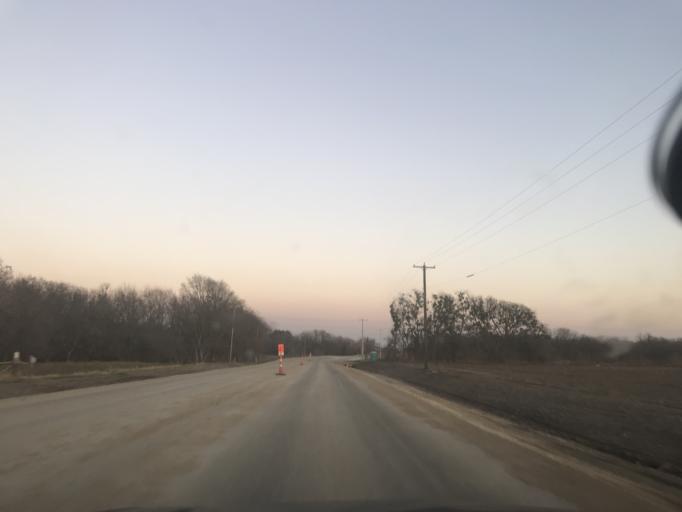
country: US
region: Texas
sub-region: Williamson County
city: Hutto
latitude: 30.5131
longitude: -97.5308
